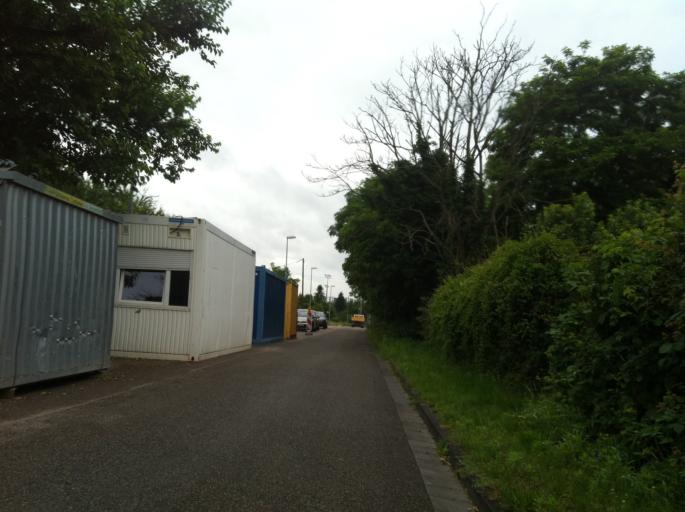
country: DE
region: Rheinland-Pfalz
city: Mainz
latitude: 50.0152
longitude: 8.2379
